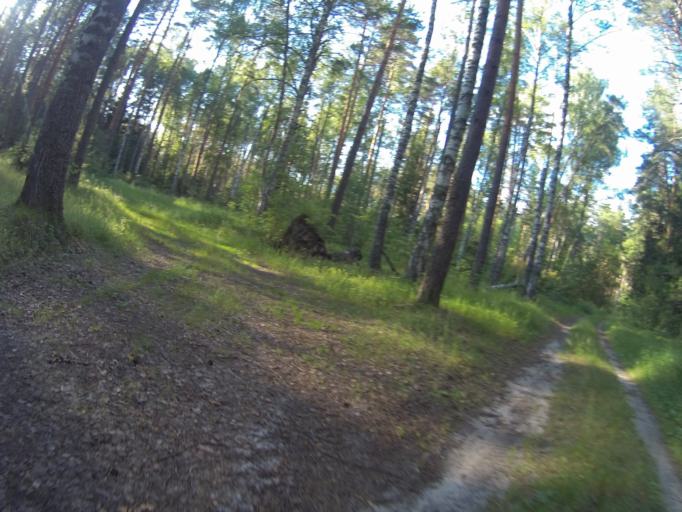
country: RU
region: Vladimir
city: Bogolyubovo
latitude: 56.1383
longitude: 40.5403
